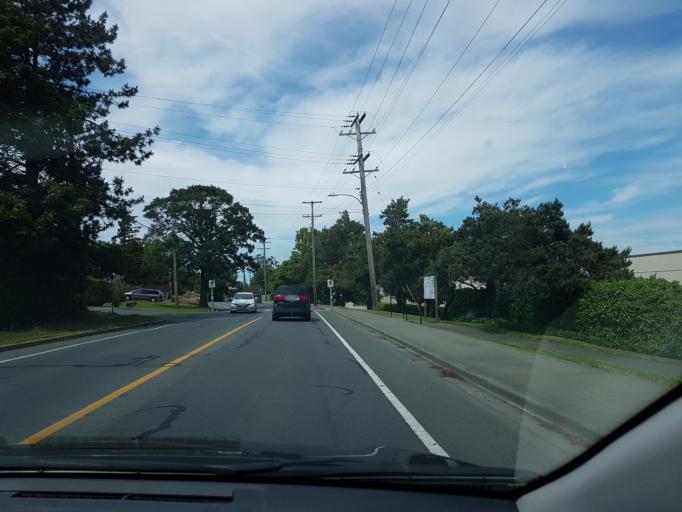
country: CA
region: British Columbia
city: Oak Bay
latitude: 48.4702
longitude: -123.3349
